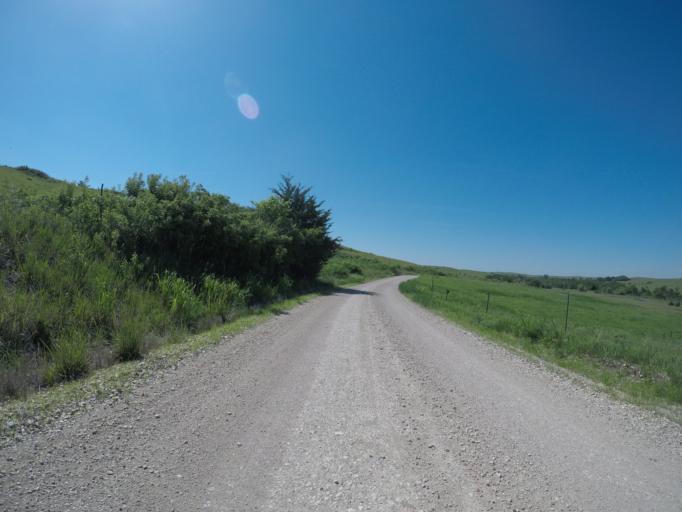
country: US
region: Kansas
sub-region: Wabaunsee County
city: Alma
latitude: 39.0160
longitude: -96.1526
